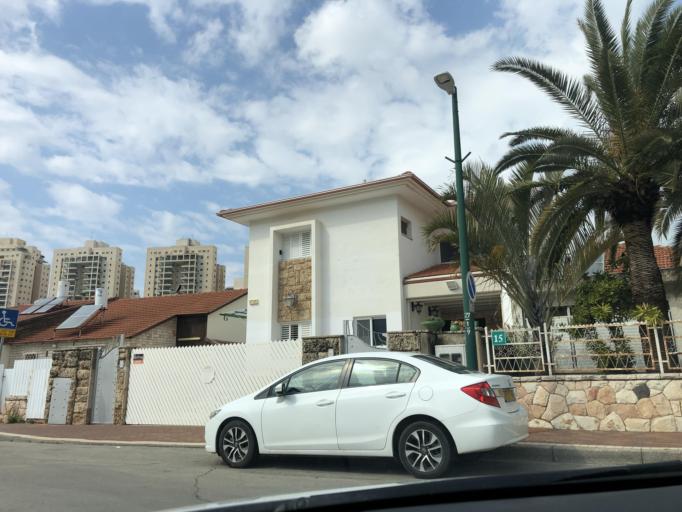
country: IL
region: Central District
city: Ganne Tiqwa
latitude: 32.0626
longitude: 34.8652
